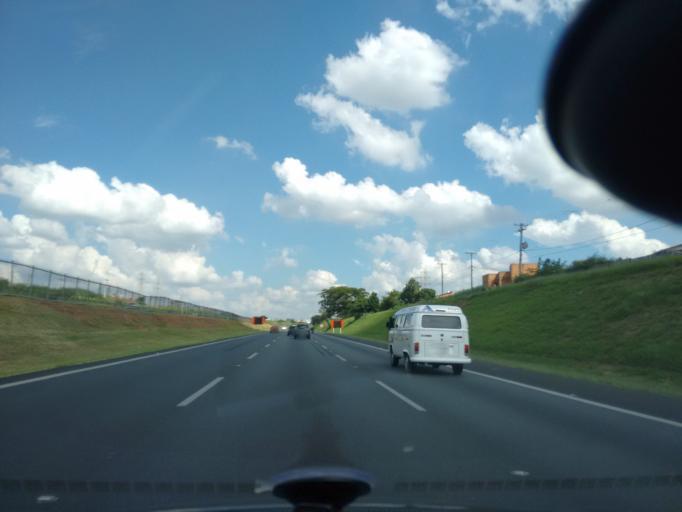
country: BR
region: Sao Paulo
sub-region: Campinas
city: Campinas
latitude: -22.9729
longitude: -47.1155
